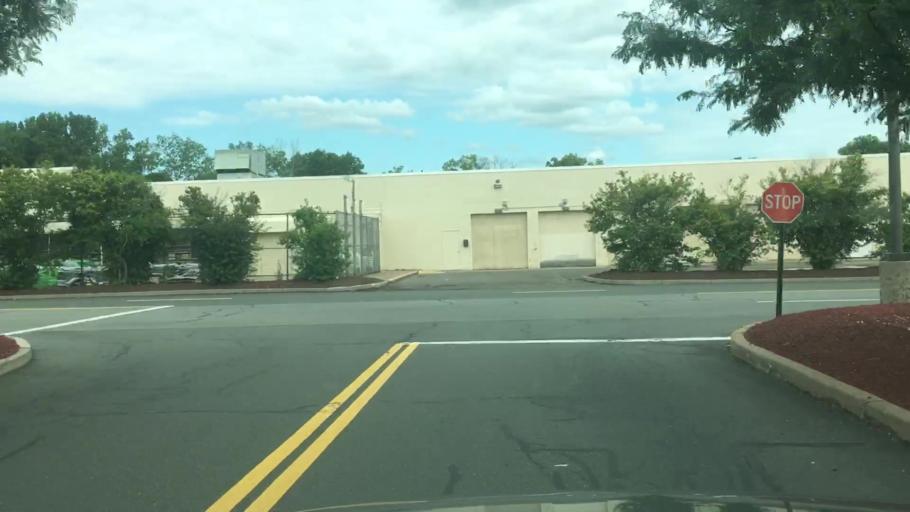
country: US
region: Connecticut
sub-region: Tolland County
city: Rockville
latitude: 41.8286
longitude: -72.4936
